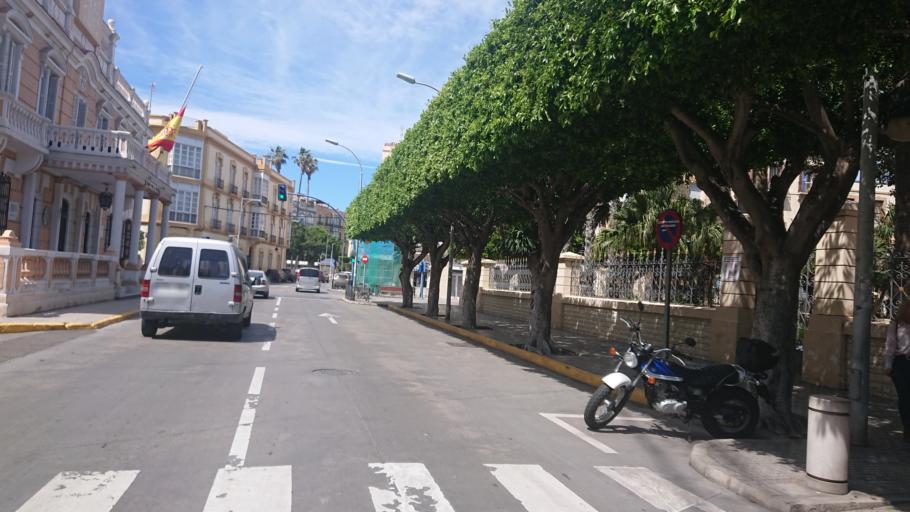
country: ES
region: Melilla
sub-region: Melilla
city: Melilla
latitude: 35.2920
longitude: -2.9427
